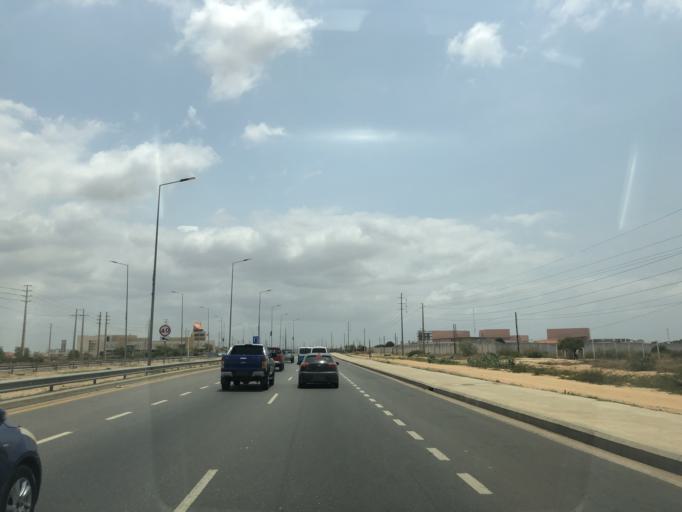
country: AO
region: Luanda
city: Luanda
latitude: -8.9564
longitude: 13.2578
